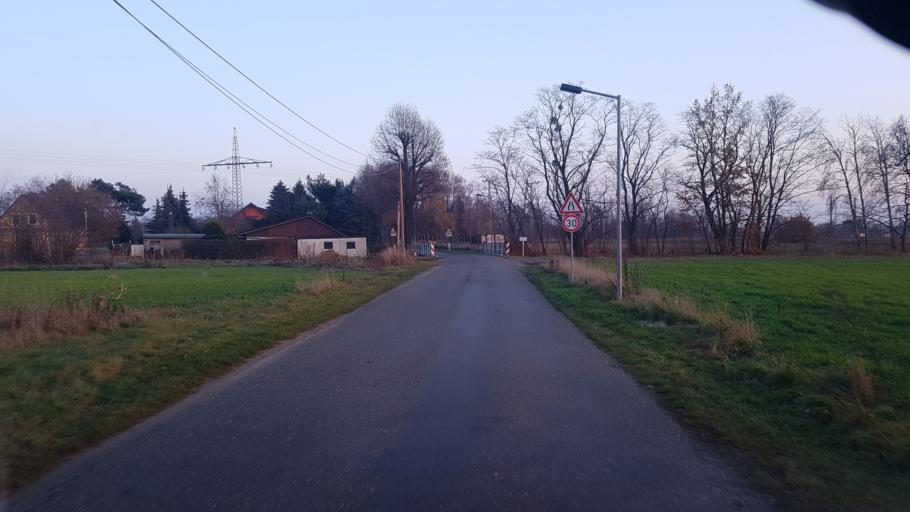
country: DE
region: Brandenburg
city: Tettau
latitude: 51.4762
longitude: 13.7227
